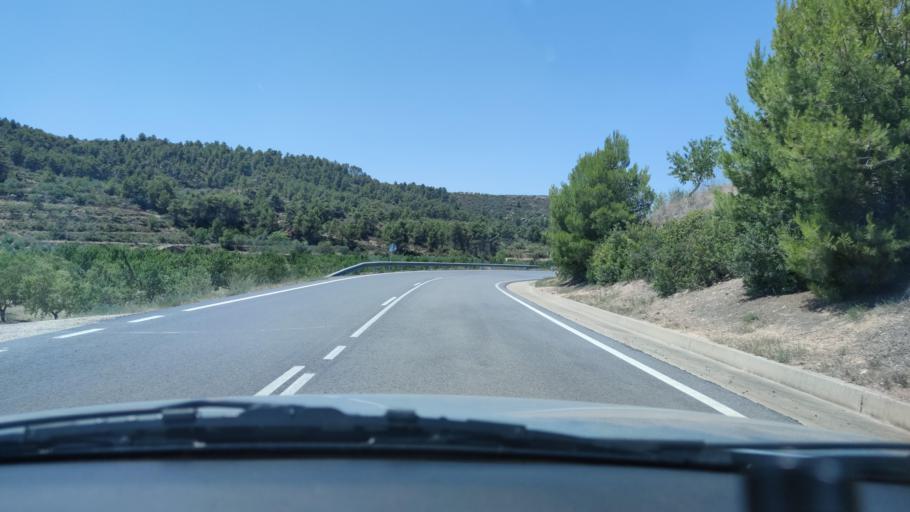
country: ES
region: Catalonia
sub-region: Provincia de Lleida
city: el Cogul
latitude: 41.4062
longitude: 0.7000
